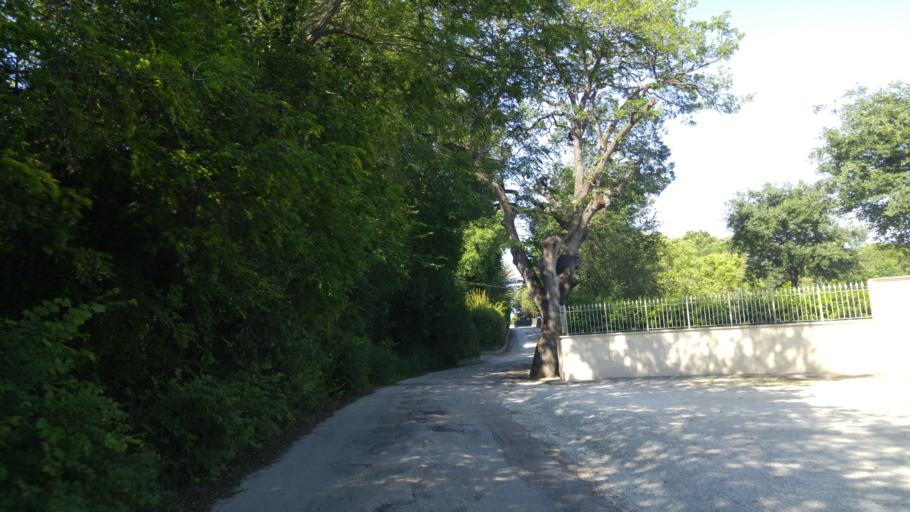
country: IT
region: The Marches
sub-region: Provincia di Pesaro e Urbino
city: Centinarola
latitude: 43.8493
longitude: 12.9931
